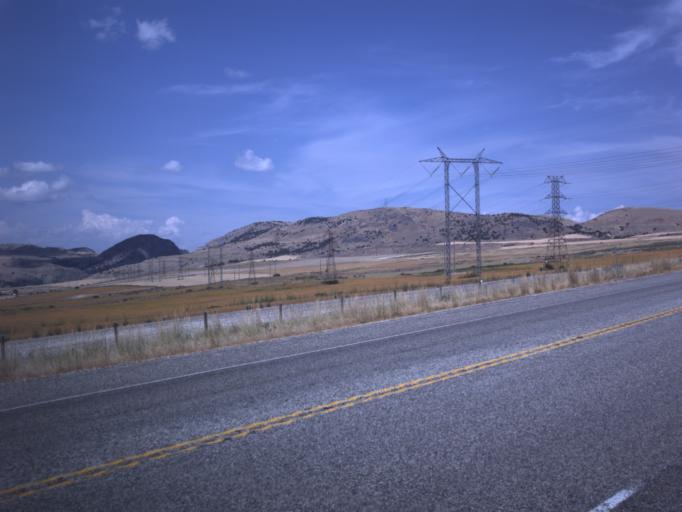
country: US
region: Utah
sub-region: Box Elder County
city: Garland
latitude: 41.7906
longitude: -112.0710
